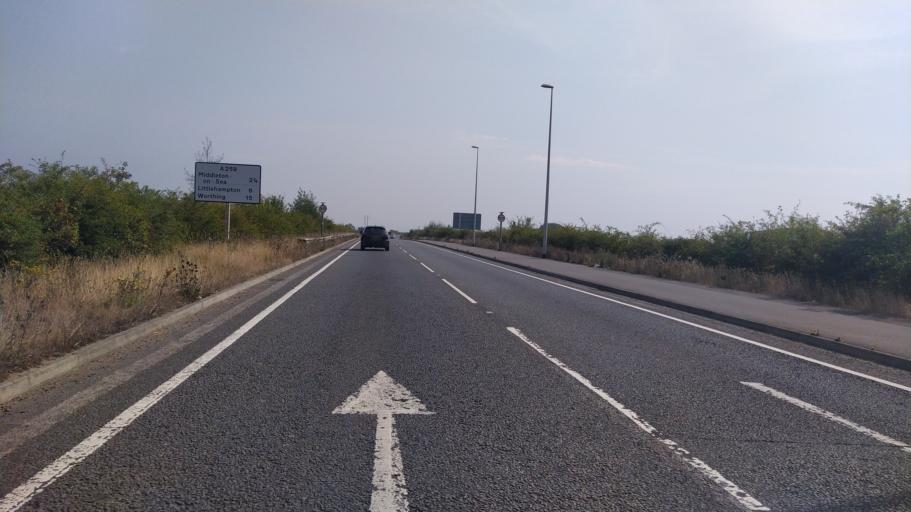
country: GB
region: England
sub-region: West Sussex
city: Bognor Regis
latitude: 50.8072
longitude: -0.6658
